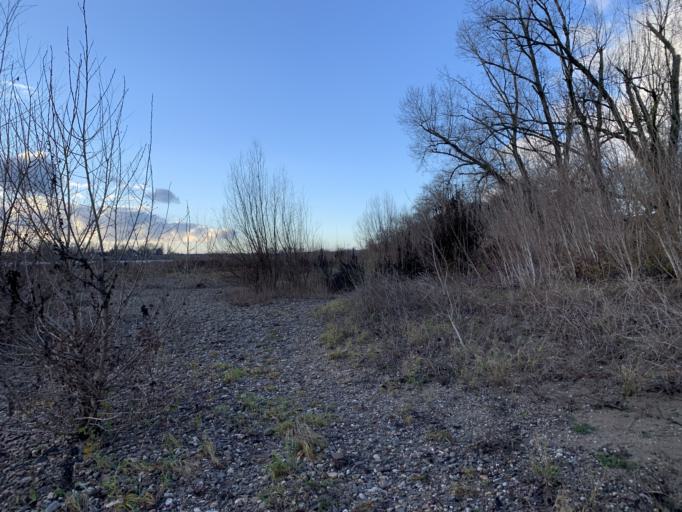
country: DE
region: North Rhine-Westphalia
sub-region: Regierungsbezirk Dusseldorf
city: Dusseldorf
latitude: 51.2564
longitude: 6.7354
